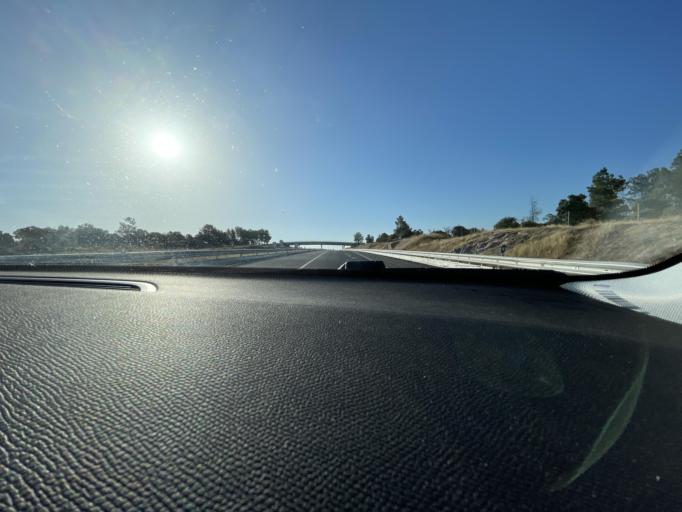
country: ES
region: Castille and Leon
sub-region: Provincia de Salamanca
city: Fuentes de Onoro
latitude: 40.6152
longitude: -6.8251
